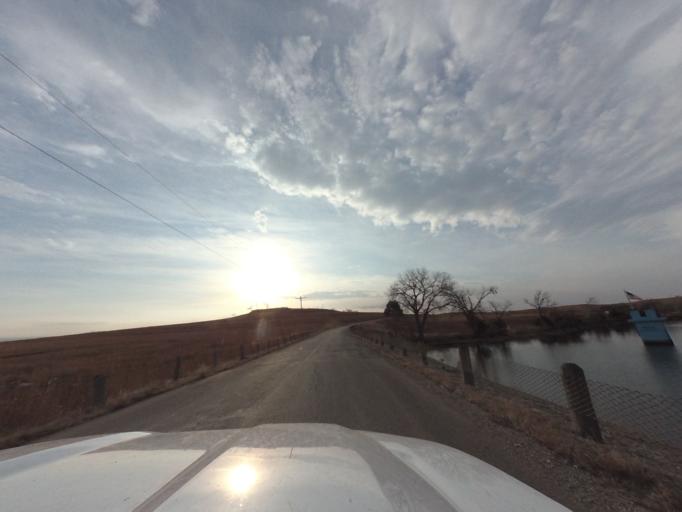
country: US
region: Kansas
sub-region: Morris County
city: Council Grove
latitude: 38.5242
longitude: -96.4121
